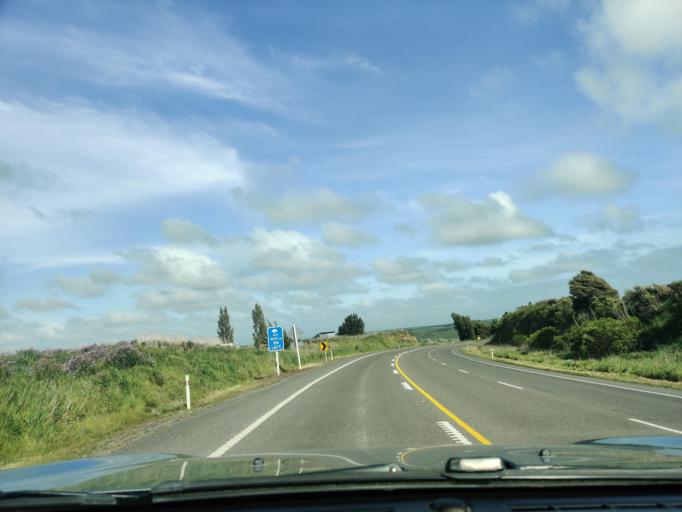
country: NZ
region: Manawatu-Wanganui
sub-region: Wanganui District
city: Wanganui
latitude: -39.9938
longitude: 175.1683
